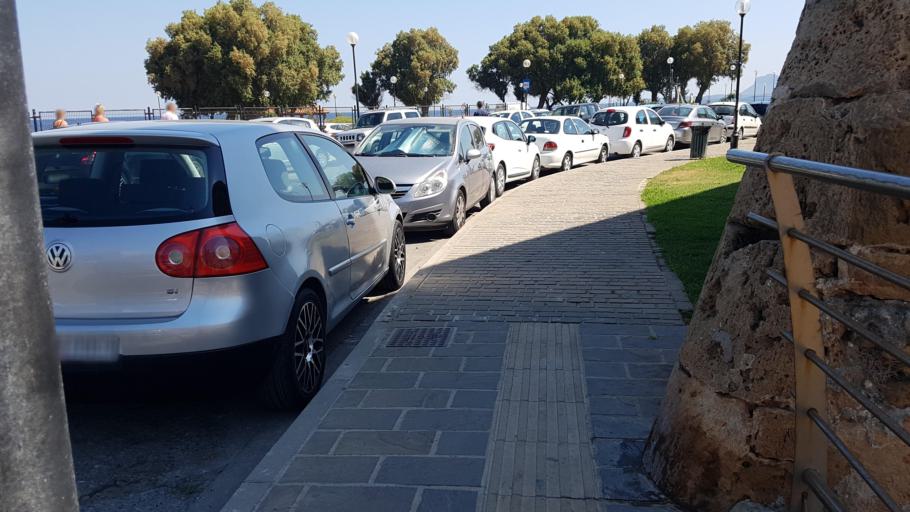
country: GR
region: Crete
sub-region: Nomos Chanias
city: Chania
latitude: 35.5182
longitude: 24.0136
